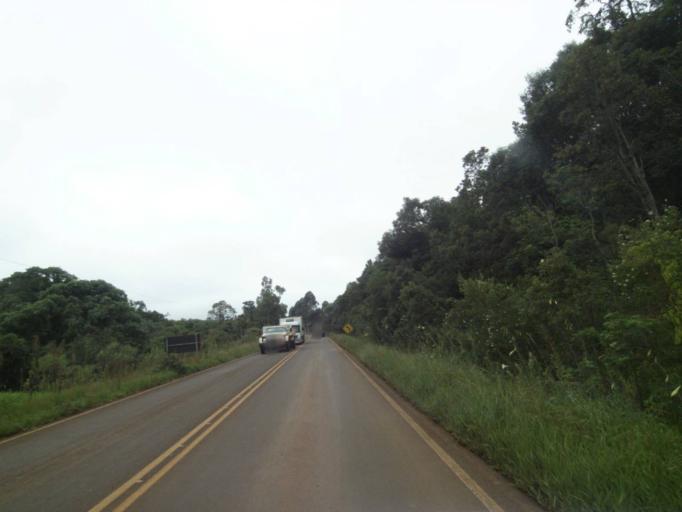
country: BR
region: Parana
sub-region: Pitanga
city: Pitanga
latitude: -24.9156
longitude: -51.8702
